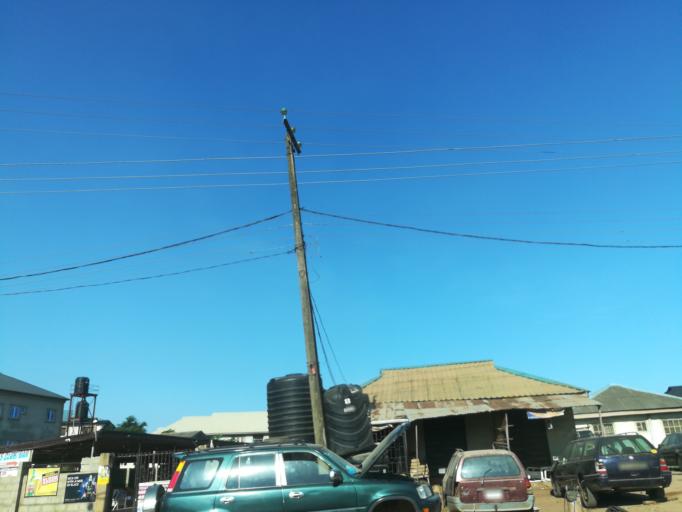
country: NG
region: Lagos
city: Ikorodu
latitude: 6.5785
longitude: 3.5264
